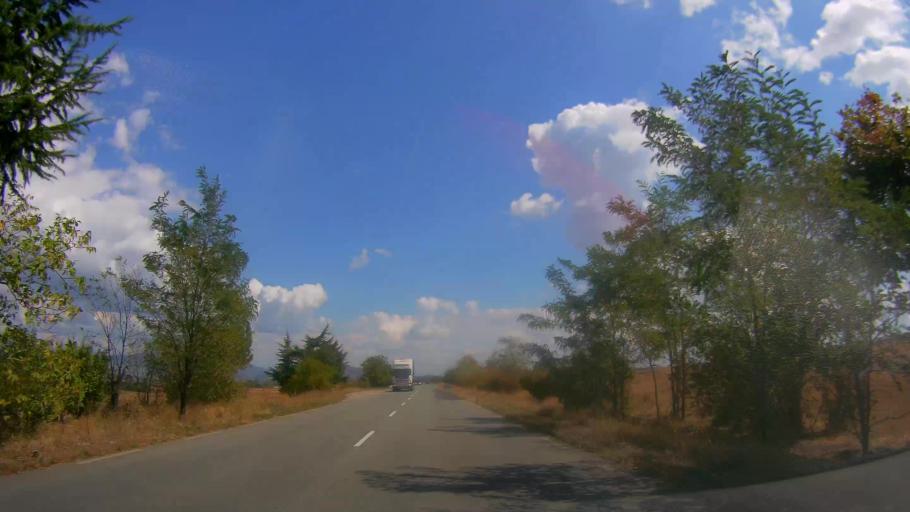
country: BG
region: Sliven
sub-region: Obshtina Tvurditsa
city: Tvurditsa
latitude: 42.6551
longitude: 25.9384
